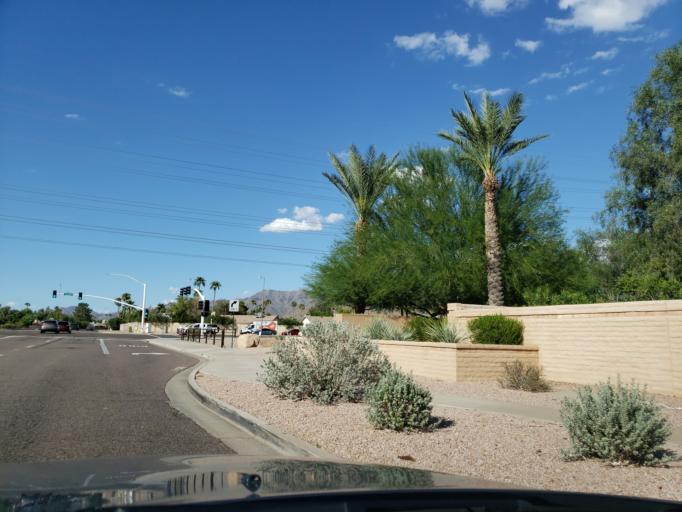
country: US
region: Arizona
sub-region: Maricopa County
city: Scottsdale
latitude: 33.5817
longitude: -111.8522
